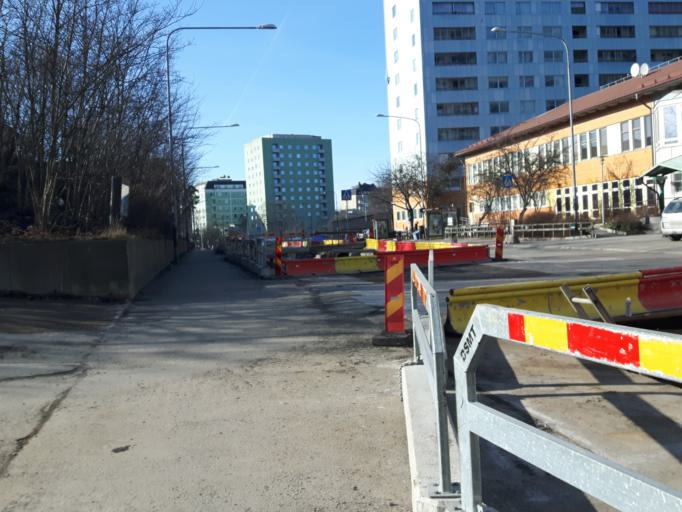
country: SE
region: Stockholm
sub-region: Solna Kommun
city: Solna
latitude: 59.3626
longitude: 18.0099
